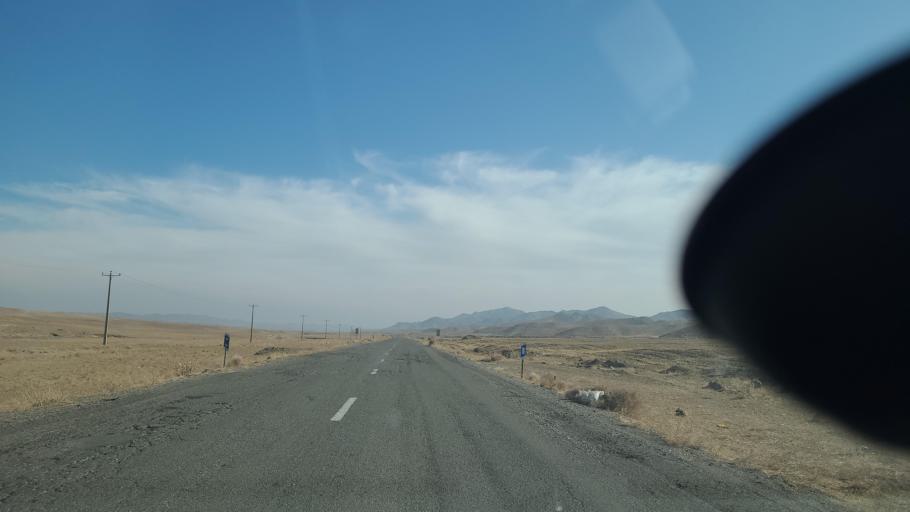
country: IR
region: Razavi Khorasan
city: Fariman
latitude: 35.5890
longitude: 59.6247
